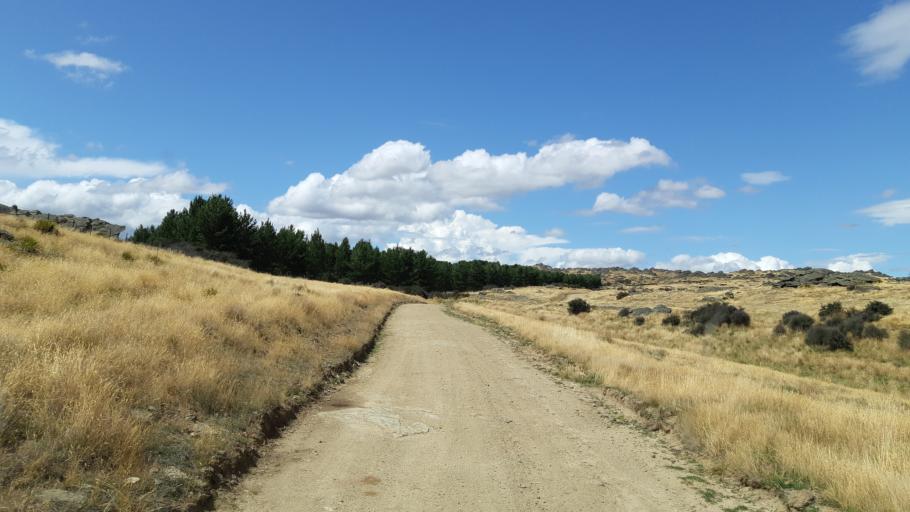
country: NZ
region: Otago
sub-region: Queenstown-Lakes District
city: Wanaka
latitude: -45.2657
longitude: 169.7146
